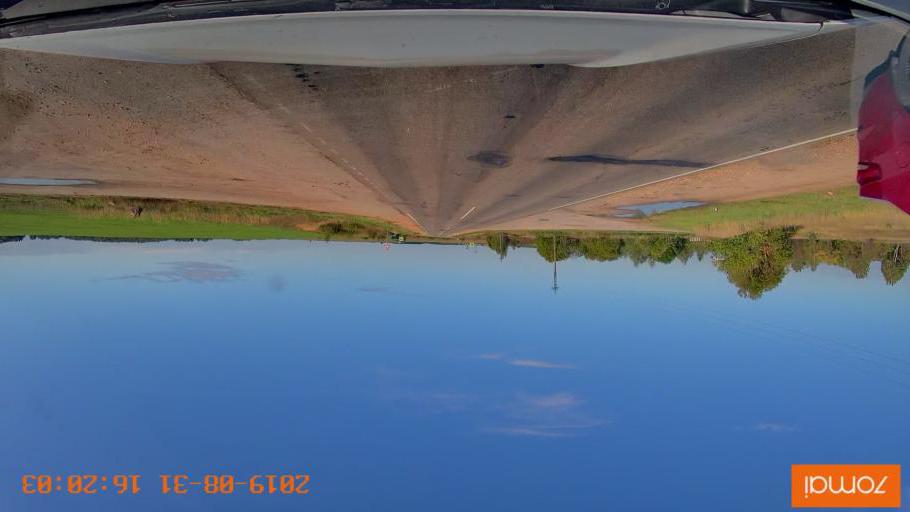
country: RU
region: Kaluga
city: Babynino
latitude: 54.5247
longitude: 35.5939
